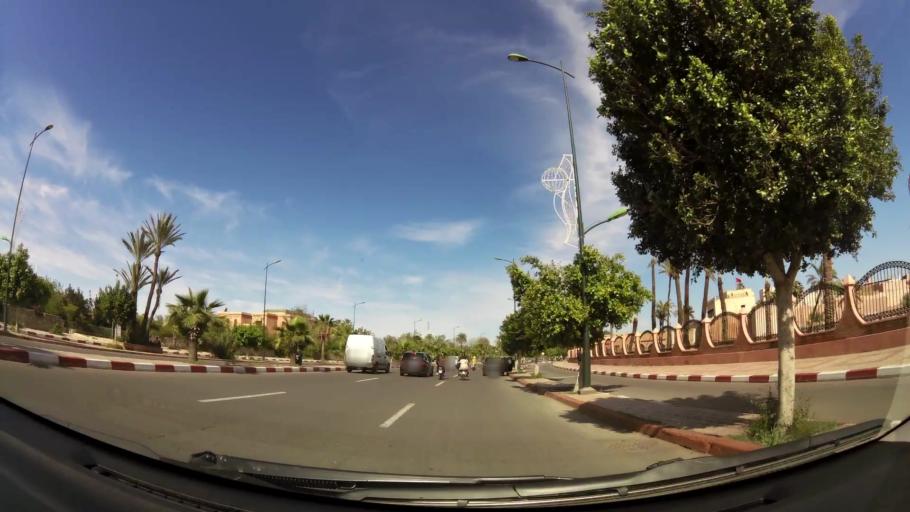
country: MA
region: Marrakech-Tensift-Al Haouz
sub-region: Marrakech
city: Marrakesh
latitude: 31.6441
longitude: -7.9933
